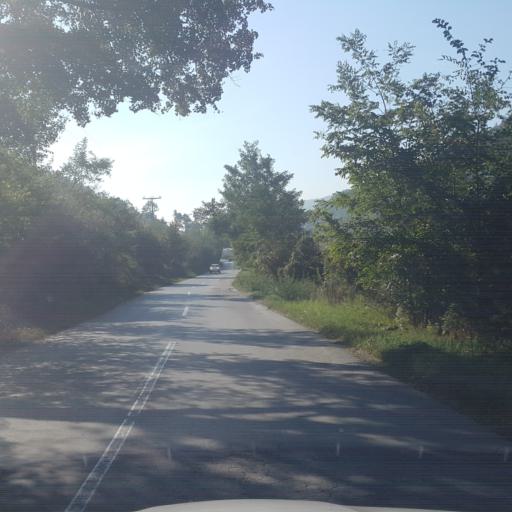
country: RS
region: Central Serbia
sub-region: Pirotski Okrug
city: Pirot
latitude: 43.2032
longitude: 22.5591
